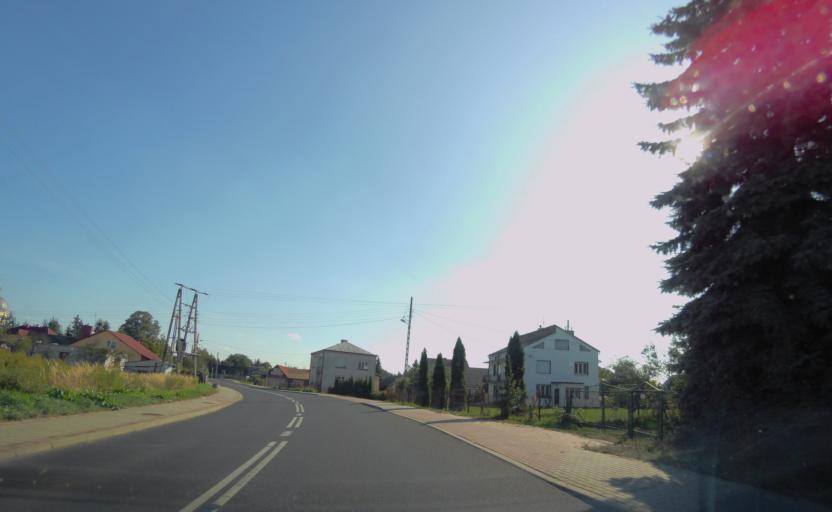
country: PL
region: Subcarpathian Voivodeship
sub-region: Powiat lezajski
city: Stare Miasto
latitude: 50.2877
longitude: 22.4285
